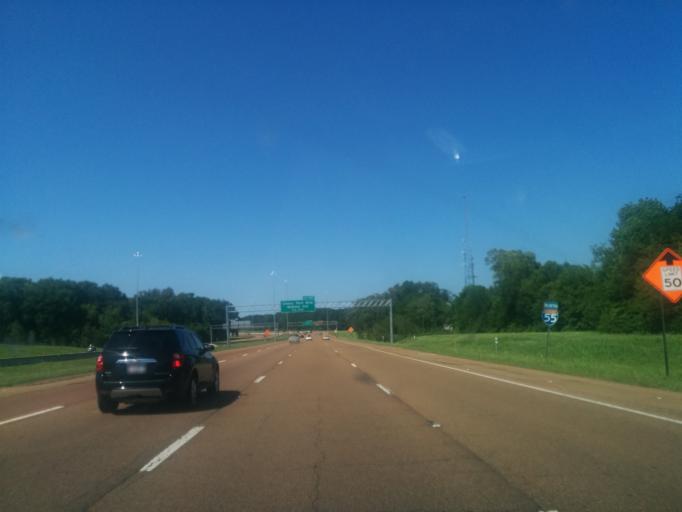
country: US
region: Mississippi
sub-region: Madison County
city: Ridgeland
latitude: 32.4190
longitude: -90.1458
